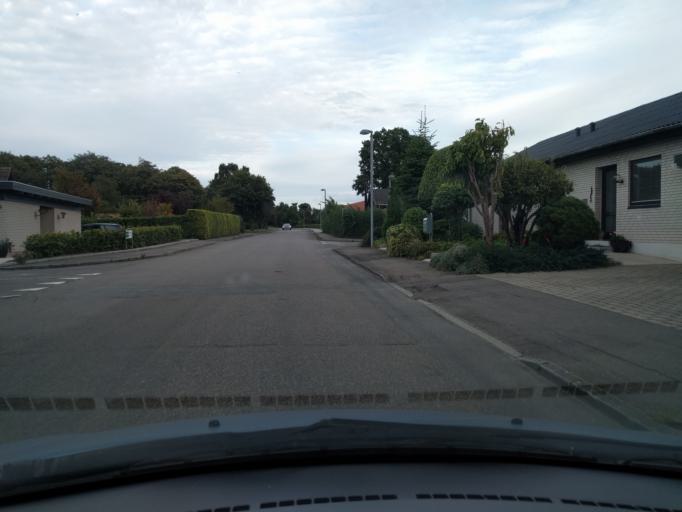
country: DK
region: Zealand
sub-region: Guldborgsund Kommune
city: Stubbekobing
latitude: 54.8914
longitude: 12.0241
